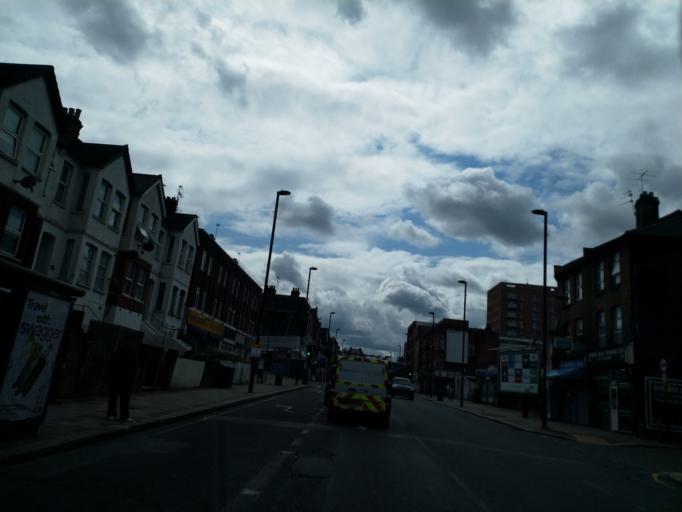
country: GB
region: England
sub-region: Greater London
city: Hendon
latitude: 51.5793
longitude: -0.2415
